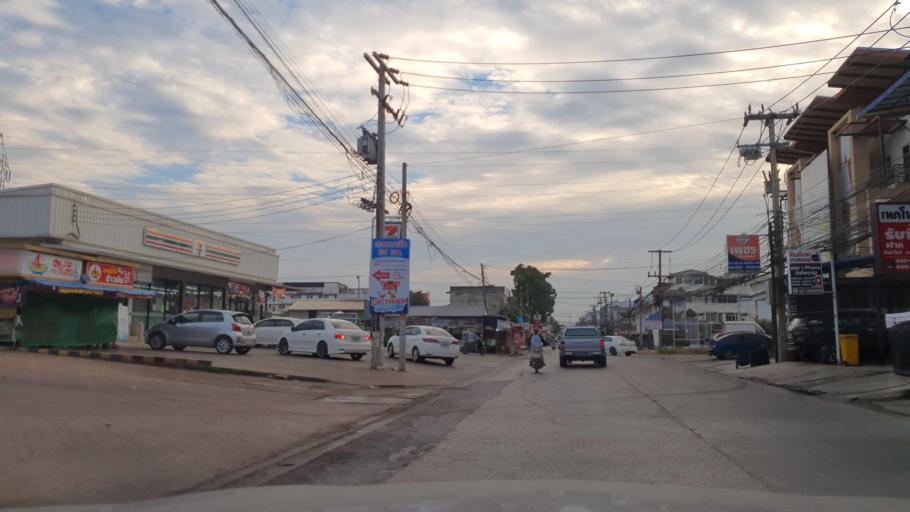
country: TH
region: Khon Kaen
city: Khon Kaen
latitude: 16.4214
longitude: 102.8130
